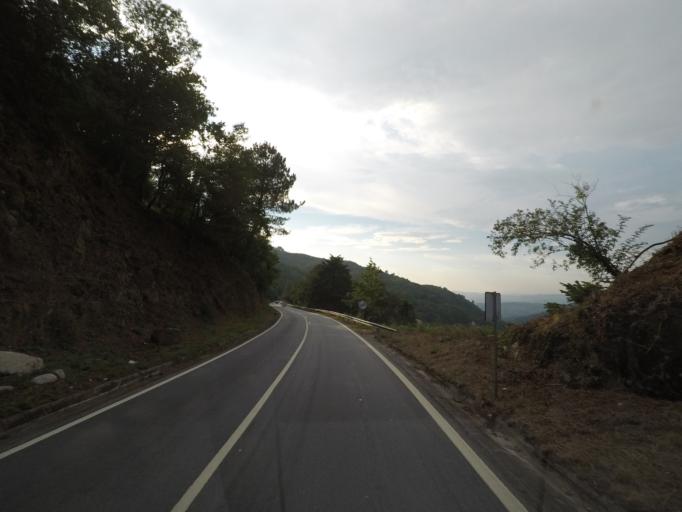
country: PT
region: Porto
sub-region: Baiao
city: Valadares
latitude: 41.2171
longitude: -7.9836
